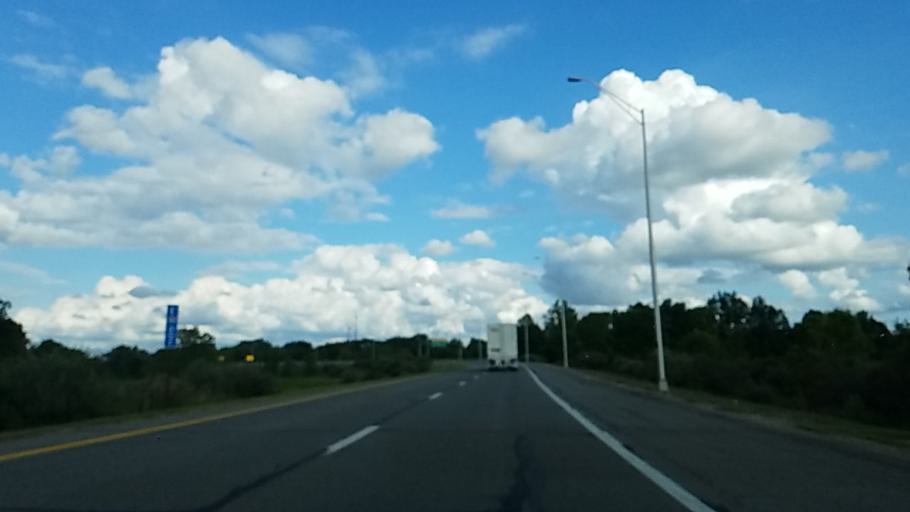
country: US
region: Ohio
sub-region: Lorain County
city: North Ridgeville
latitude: 41.3784
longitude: -82.0029
